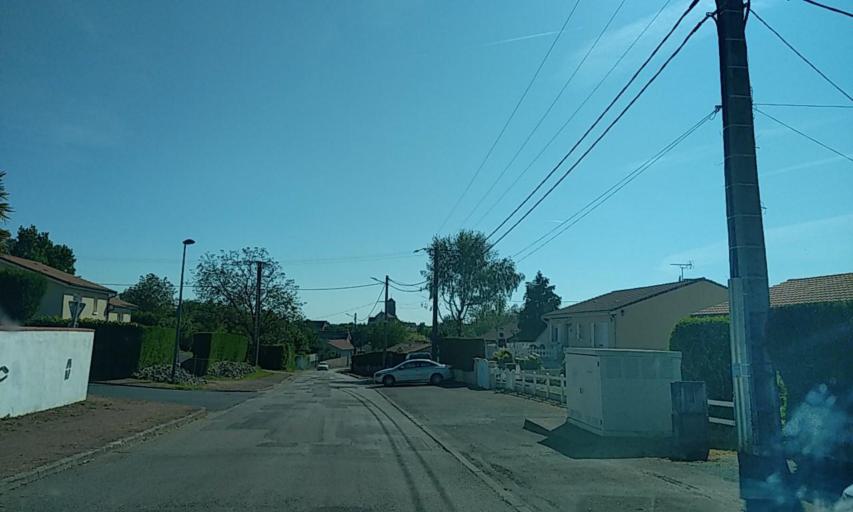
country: FR
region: Poitou-Charentes
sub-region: Departement des Deux-Sevres
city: Boisme
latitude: 46.7768
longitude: -0.4308
